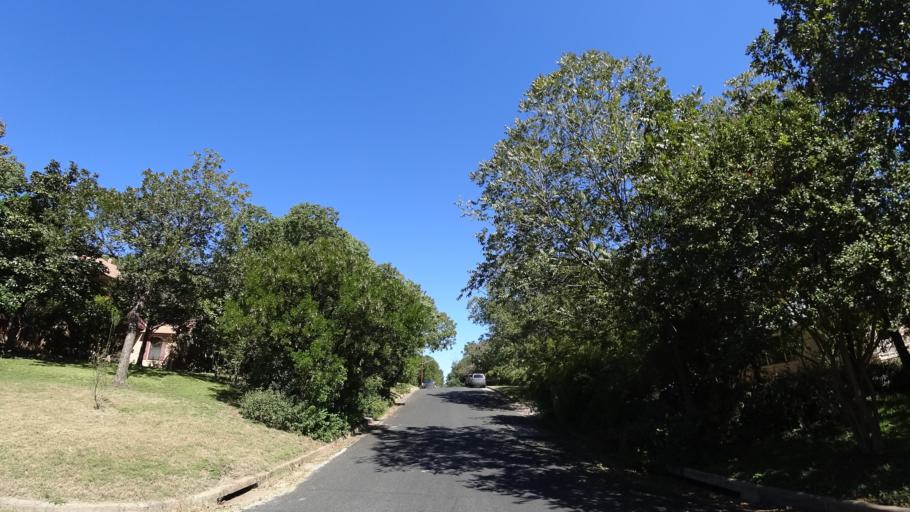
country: US
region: Texas
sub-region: Travis County
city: Austin
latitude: 30.2399
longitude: -97.7428
